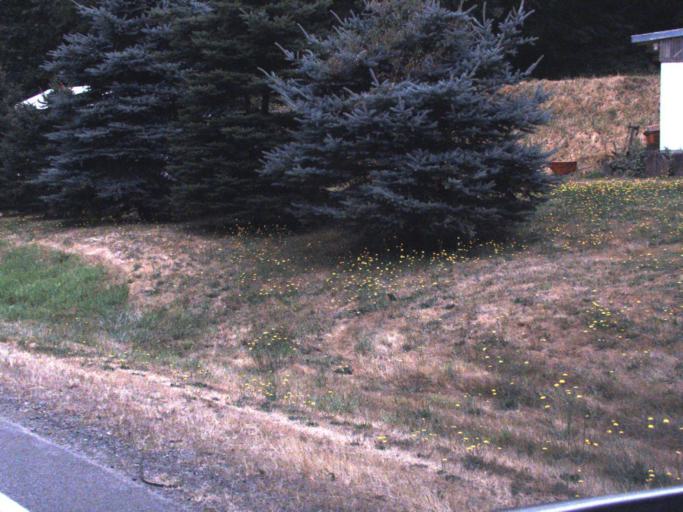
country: US
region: Washington
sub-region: King County
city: Duvall
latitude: 47.7692
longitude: -121.9557
